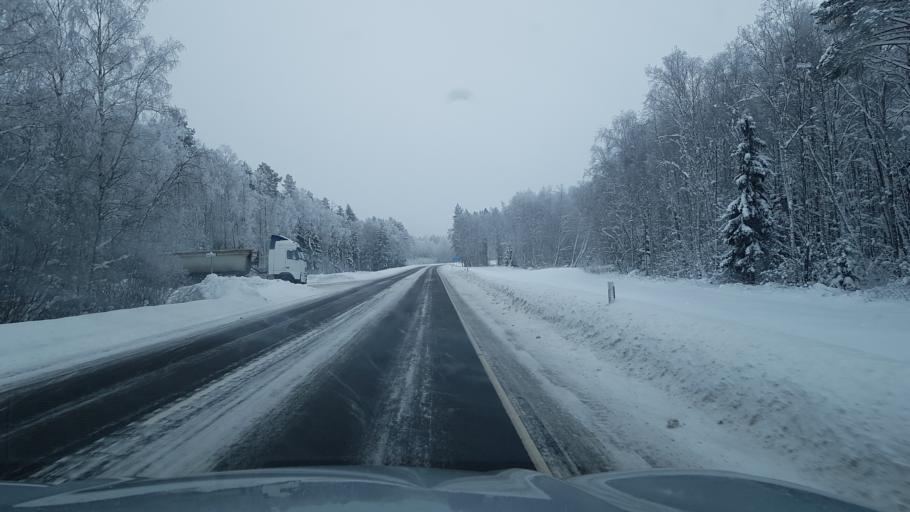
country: EE
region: Ida-Virumaa
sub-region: Johvi vald
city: Johvi
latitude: 59.2966
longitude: 27.3975
